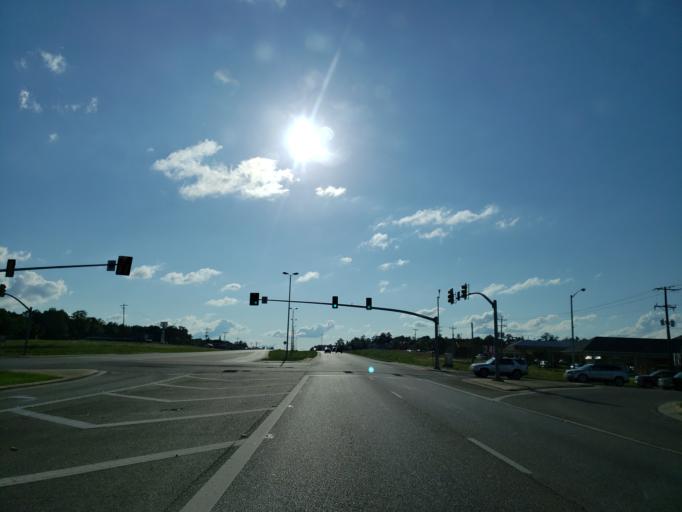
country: US
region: Mississippi
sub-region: Forrest County
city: Petal
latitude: 31.3507
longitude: -89.2332
